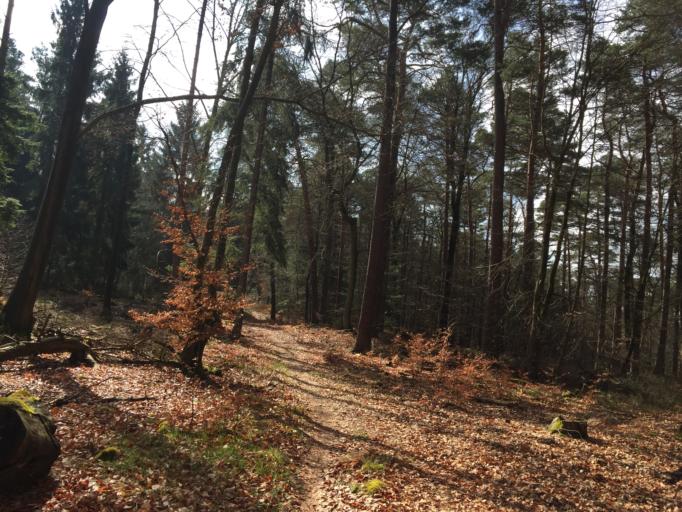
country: DE
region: Rheinland-Pfalz
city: Frankenstein
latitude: 49.4129
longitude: 7.9507
